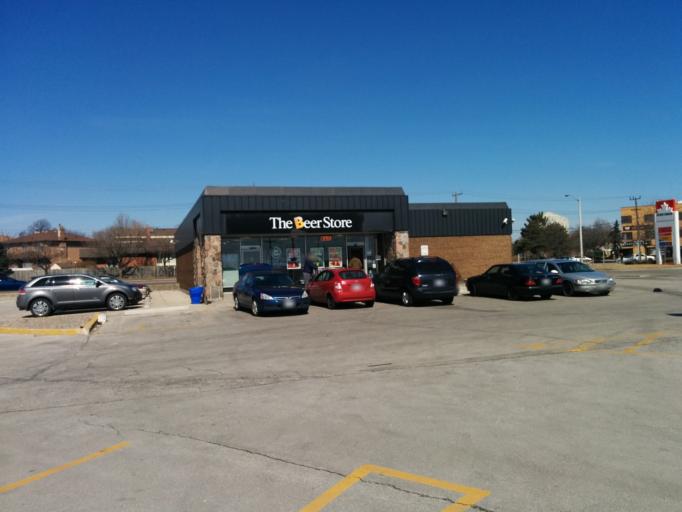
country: CA
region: Ontario
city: Etobicoke
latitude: 43.6310
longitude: -79.5518
